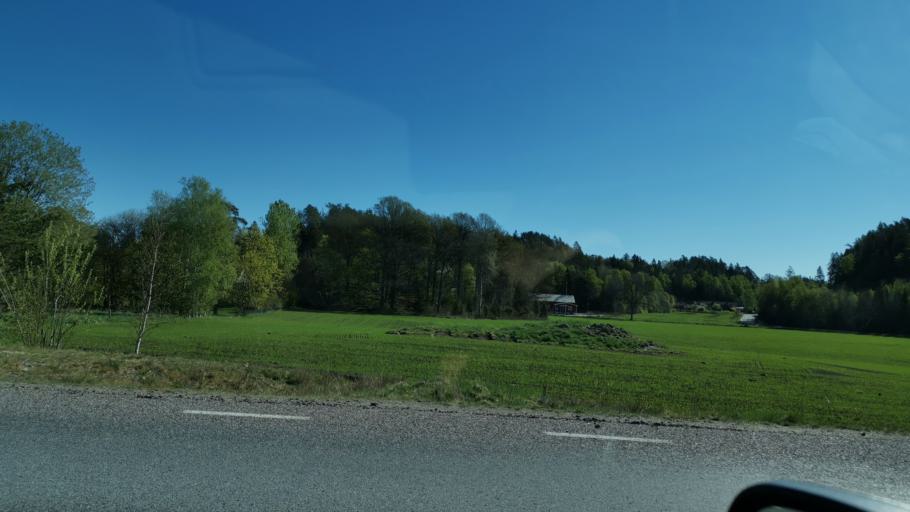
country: SE
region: Vaestra Goetaland
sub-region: Uddevalla Kommun
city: Uddevalla
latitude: 58.2969
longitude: 11.8972
